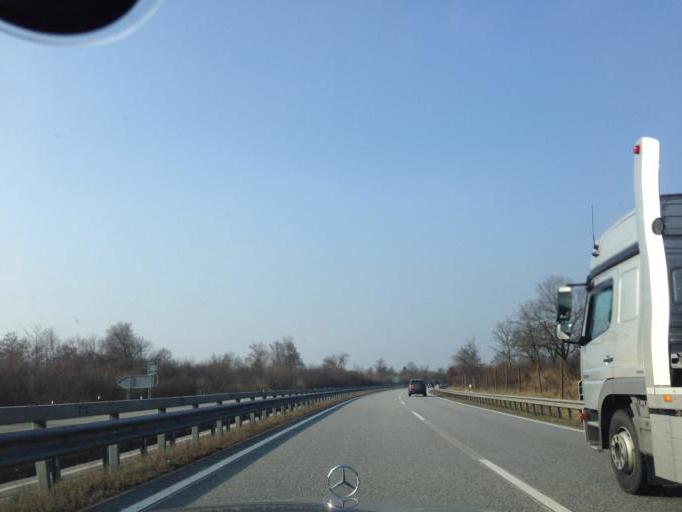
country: DE
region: Schleswig-Holstein
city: Negernbotel
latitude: 53.9704
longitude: 10.2432
